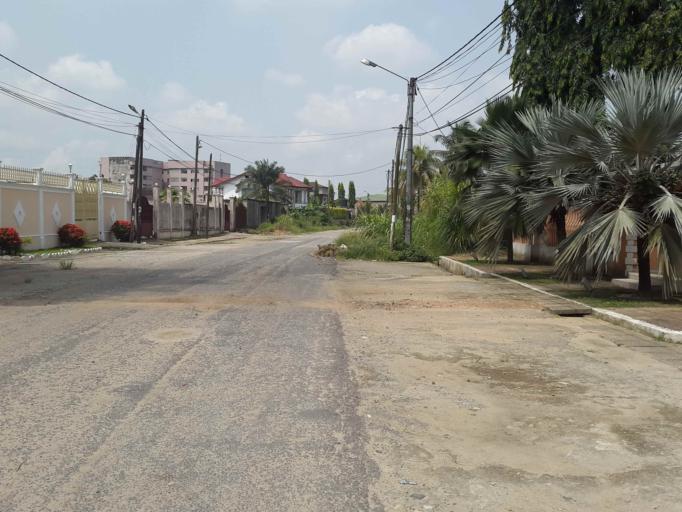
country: CM
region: Littoral
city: Douala
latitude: 4.0894
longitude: 9.7353
